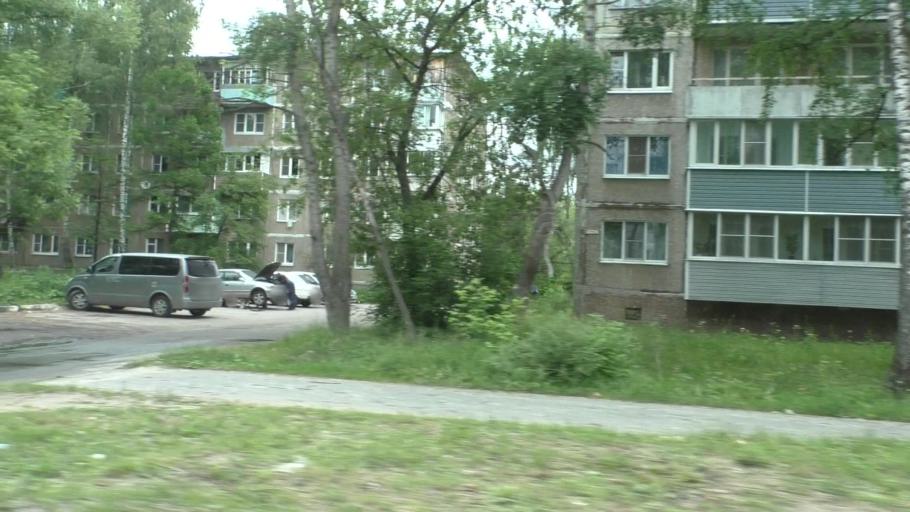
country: RU
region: Moskovskaya
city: Yegor'yevsk
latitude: 55.3686
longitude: 39.0541
